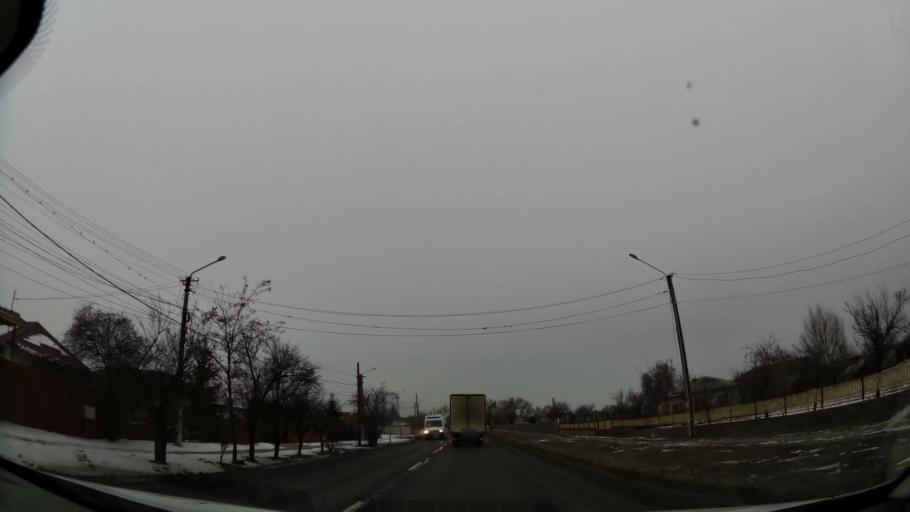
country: RO
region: Dambovita
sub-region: Comuna Racari
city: Racari
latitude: 44.6216
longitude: 25.7523
